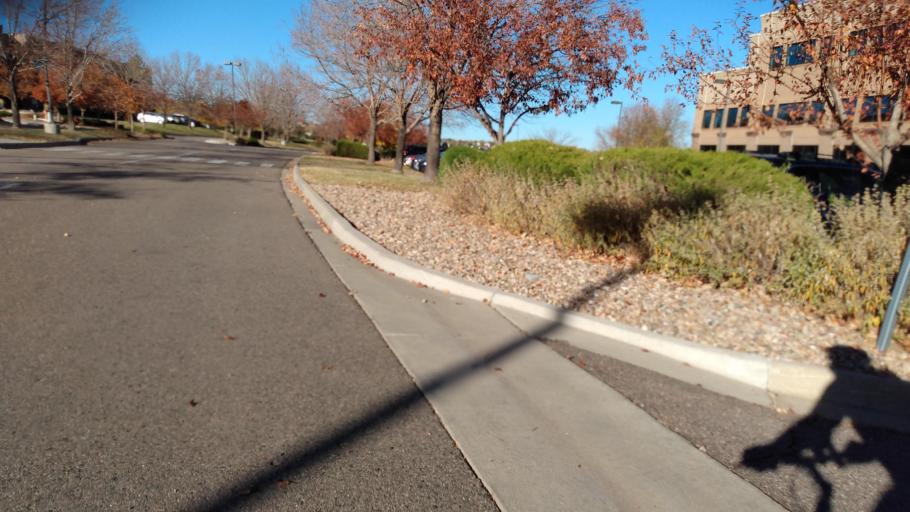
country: US
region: Colorado
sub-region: Boulder County
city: Superior
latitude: 39.9627
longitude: -105.1701
